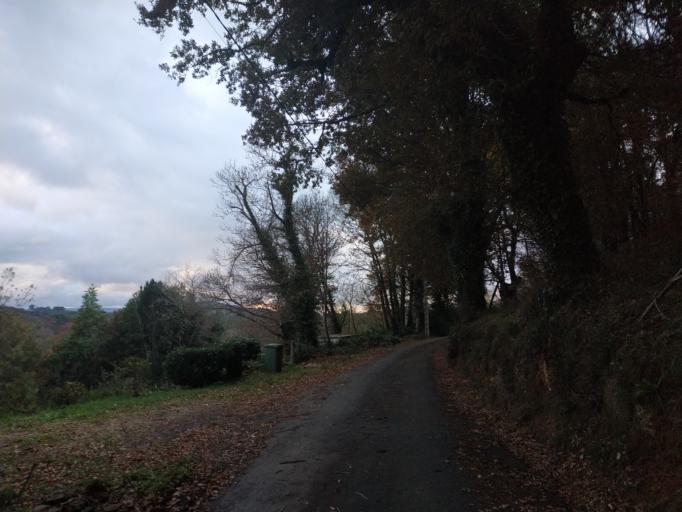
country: ES
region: Galicia
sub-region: Provincia de Pontevedra
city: Silleda
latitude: 42.7833
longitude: -8.1667
